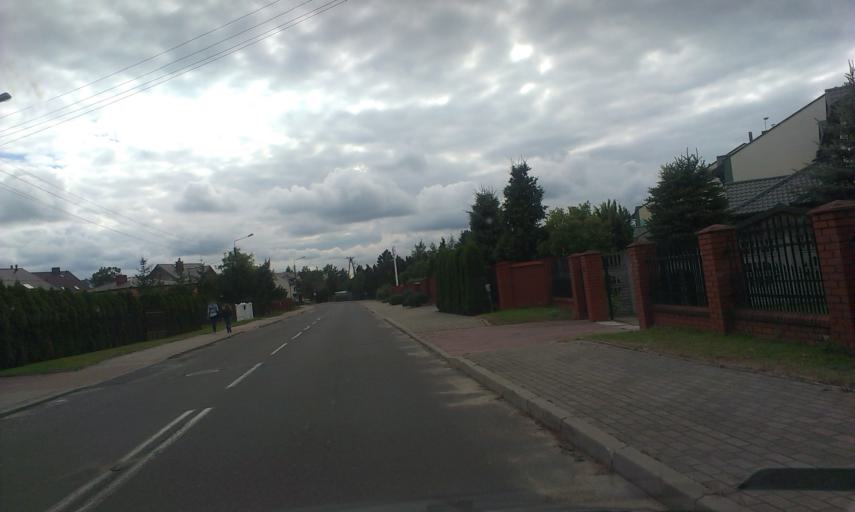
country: PL
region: Masovian Voivodeship
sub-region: Powiat zyrardowski
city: Mszczonow
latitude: 51.9753
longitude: 20.5294
